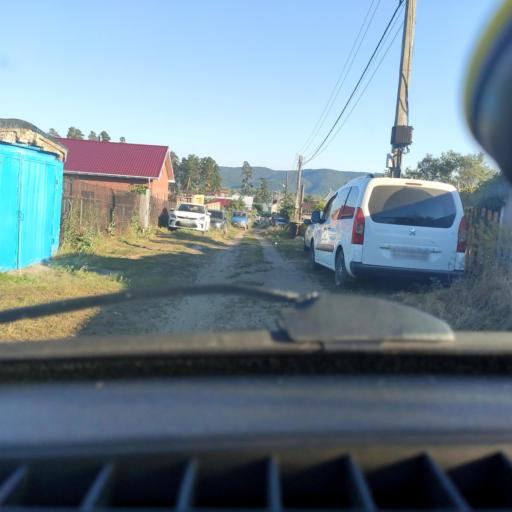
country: RU
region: Samara
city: Zhigulevsk
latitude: 53.4710
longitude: 49.5914
